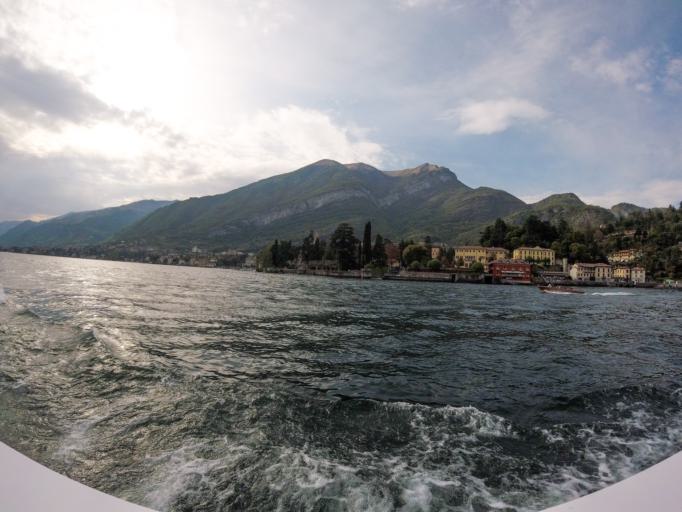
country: IT
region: Lombardy
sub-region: Provincia di Como
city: Tremezzo
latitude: 45.9805
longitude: 9.2238
